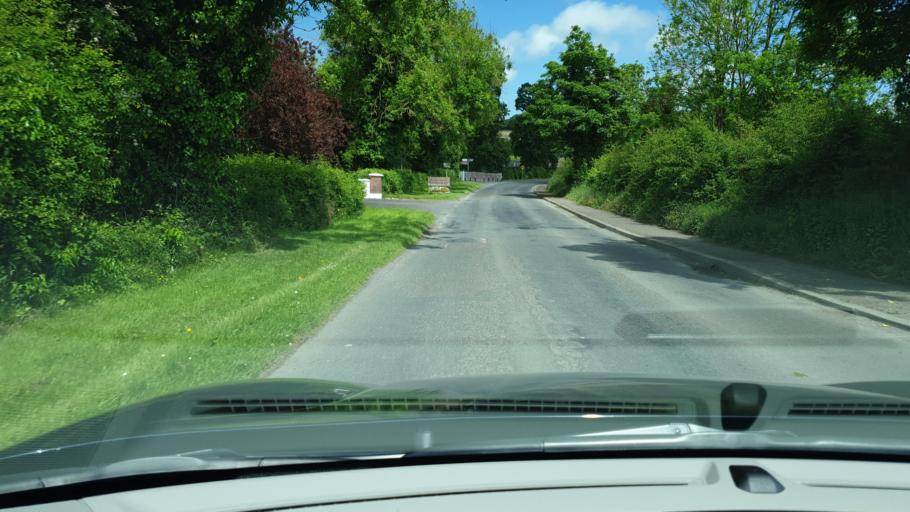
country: IE
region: Leinster
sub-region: Lu
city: Ardee
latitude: 53.8481
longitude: -6.6548
